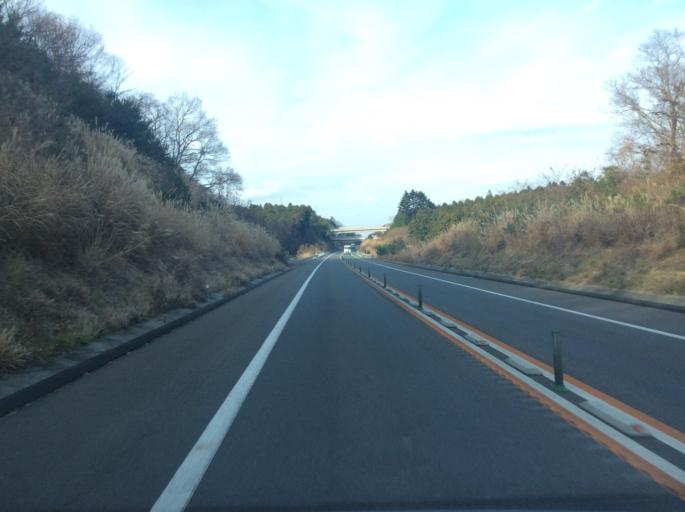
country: JP
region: Fukushima
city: Namie
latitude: 37.3228
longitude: 140.9908
